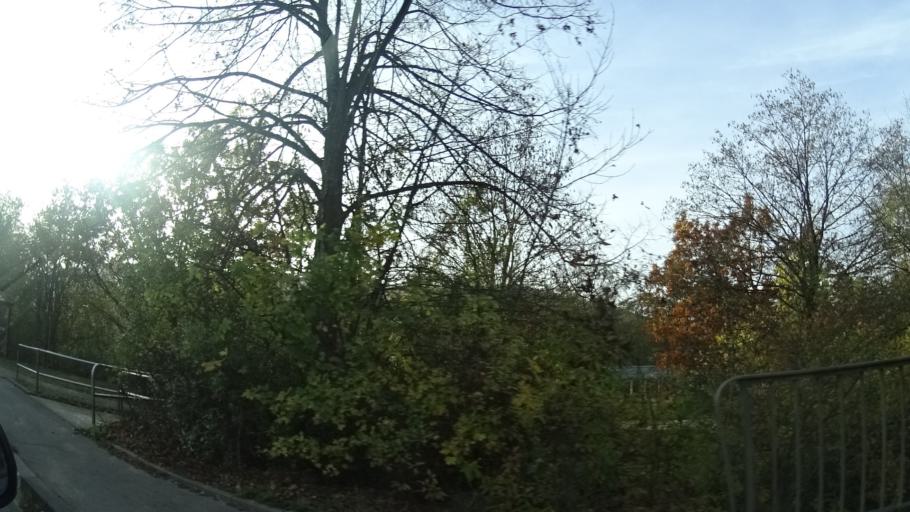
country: DE
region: Baden-Wuerttemberg
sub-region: Karlsruhe Region
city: Mosbach
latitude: 49.3653
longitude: 9.1521
